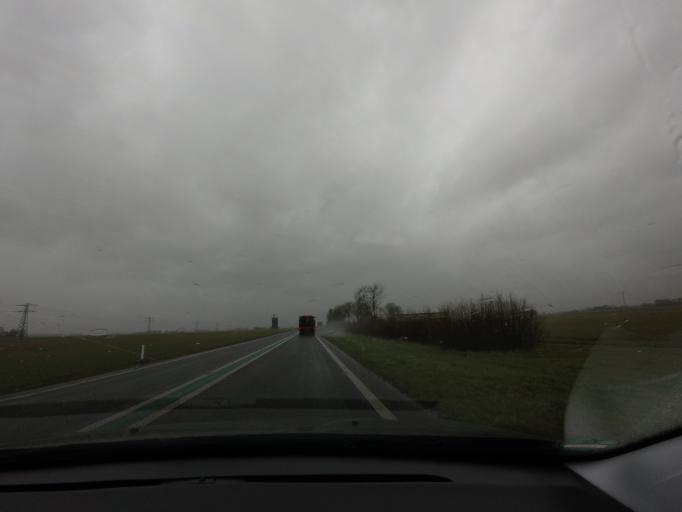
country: NL
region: Friesland
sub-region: Sudwest Fryslan
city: Bolsward
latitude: 53.0715
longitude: 5.5105
